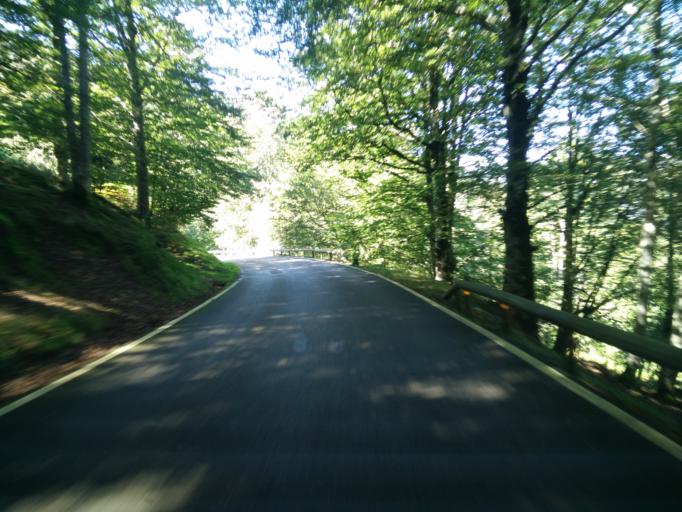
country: ES
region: Cantabria
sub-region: Provincia de Cantabria
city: Ruente
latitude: 43.1019
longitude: -4.2736
